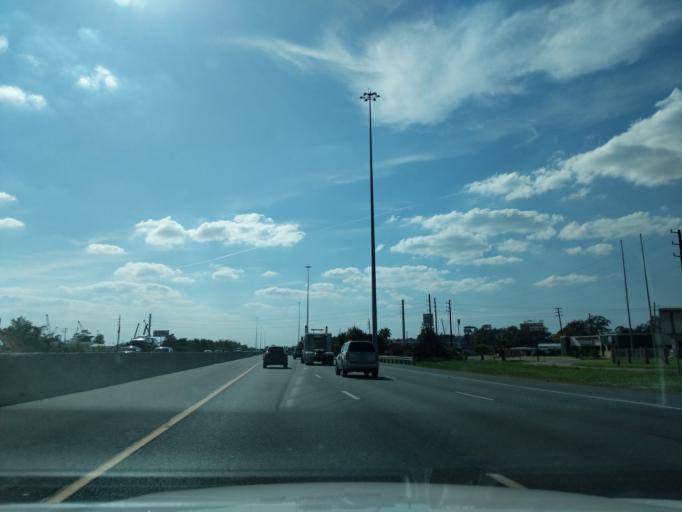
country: US
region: Texas
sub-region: Harris County
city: Channelview
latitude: 29.7888
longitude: -95.0935
